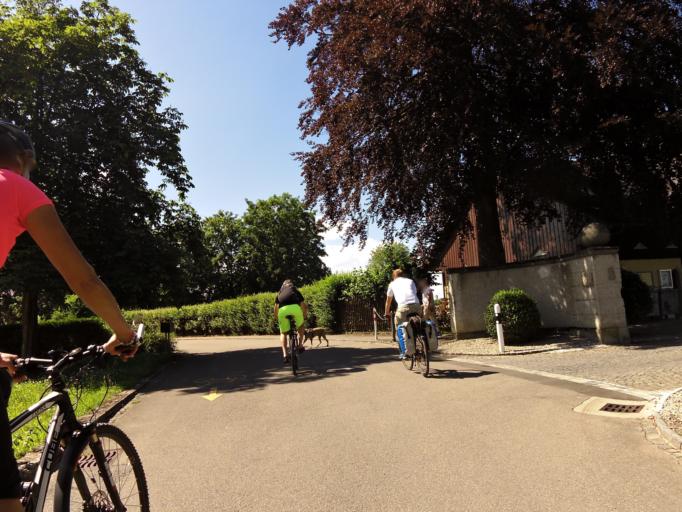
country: CH
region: Thurgau
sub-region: Arbon District
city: Arbon
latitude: 47.5043
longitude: 9.4440
